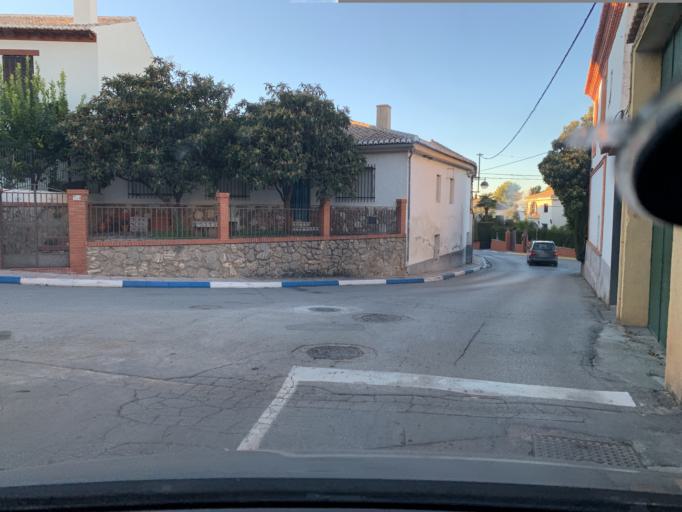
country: ES
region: Andalusia
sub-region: Provincia de Granada
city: Dilar
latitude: 37.0767
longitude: -3.6027
